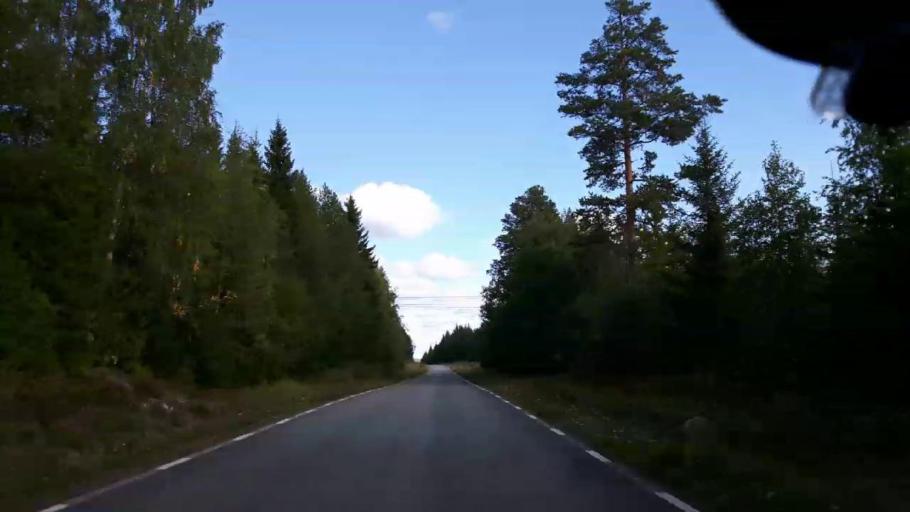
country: SE
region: Jaemtland
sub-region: OEstersunds Kommun
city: Brunflo
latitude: 63.2008
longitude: 15.2271
